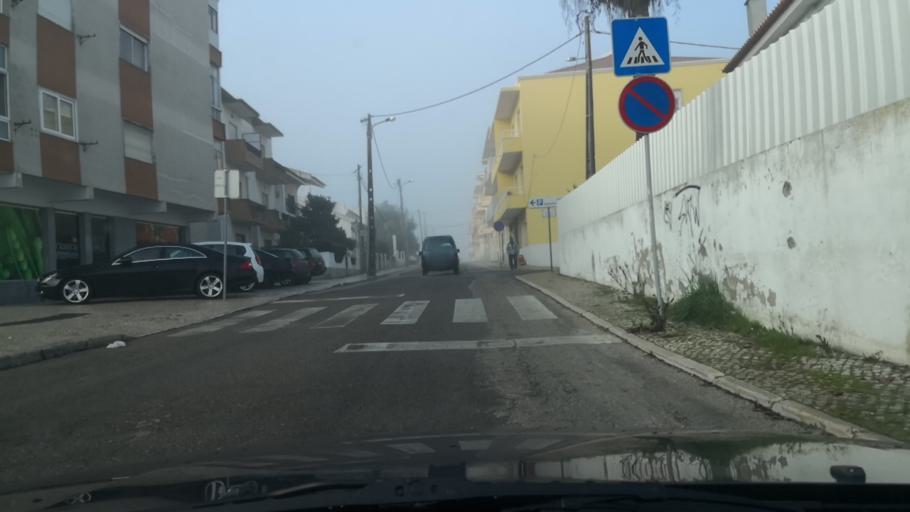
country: PT
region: Setubal
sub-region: Palmela
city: Pinhal Novo
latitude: 38.6372
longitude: -8.9148
